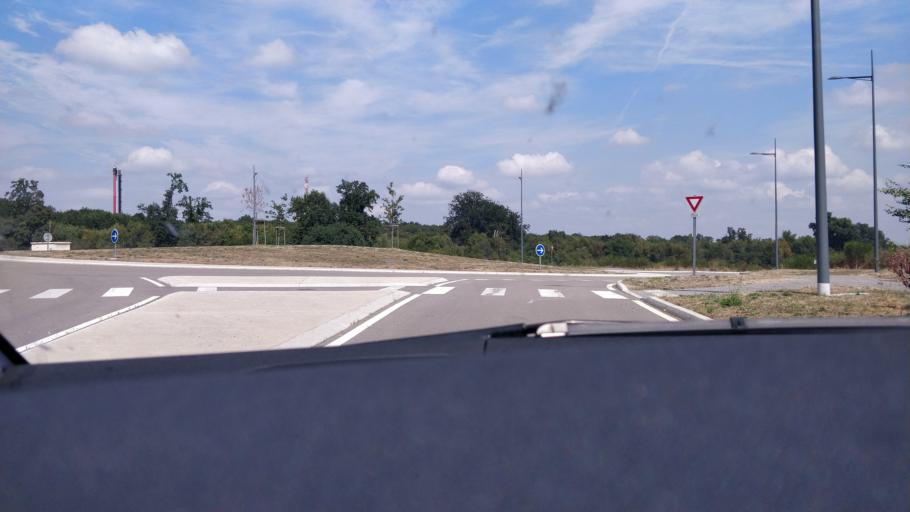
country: FR
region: Limousin
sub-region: Departement de la Haute-Vienne
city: Le Palais-sur-Vienne
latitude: 45.8631
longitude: 1.2997
